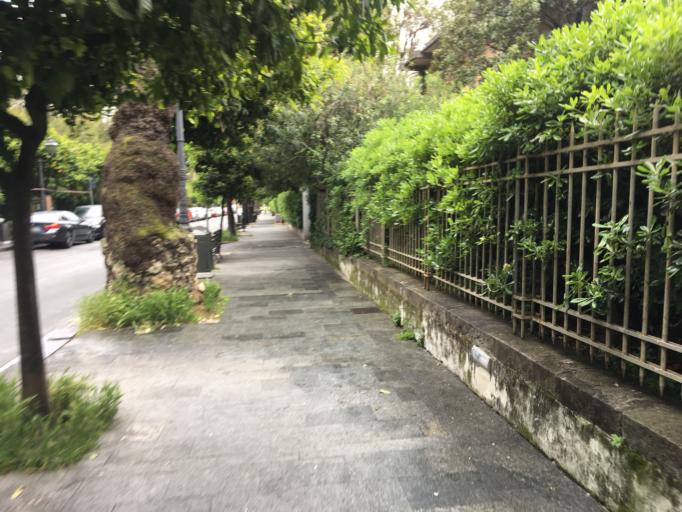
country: IT
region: Liguria
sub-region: Provincia di Genova
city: Bogliasco
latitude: 44.3830
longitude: 9.0401
